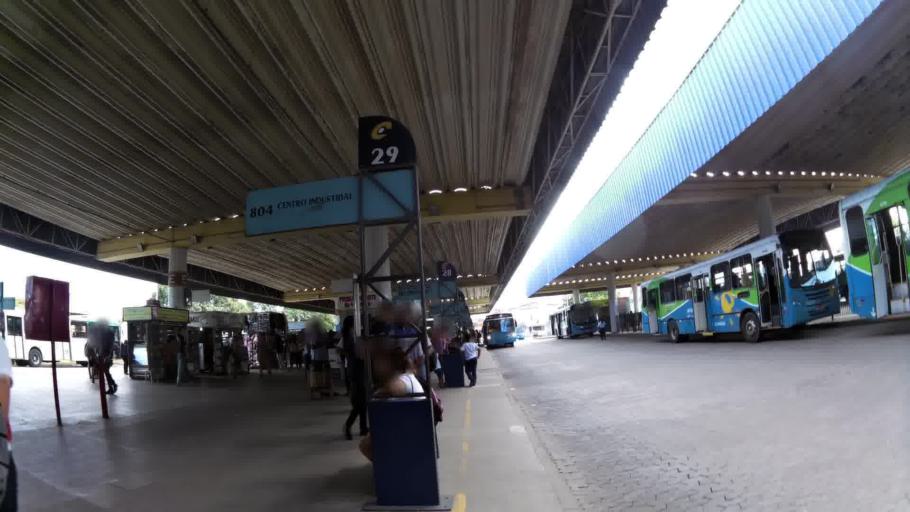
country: BR
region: Espirito Santo
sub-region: Serra
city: Serra
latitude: -20.1932
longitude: -40.2557
